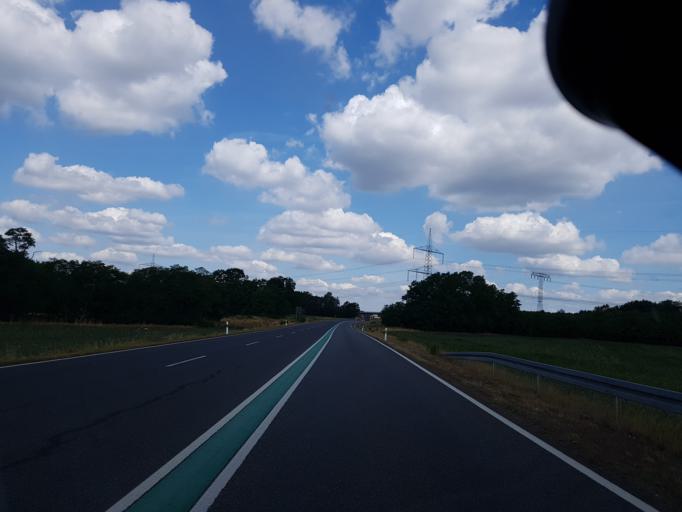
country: DE
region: Brandenburg
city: Drebkau
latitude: 51.6581
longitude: 14.2426
